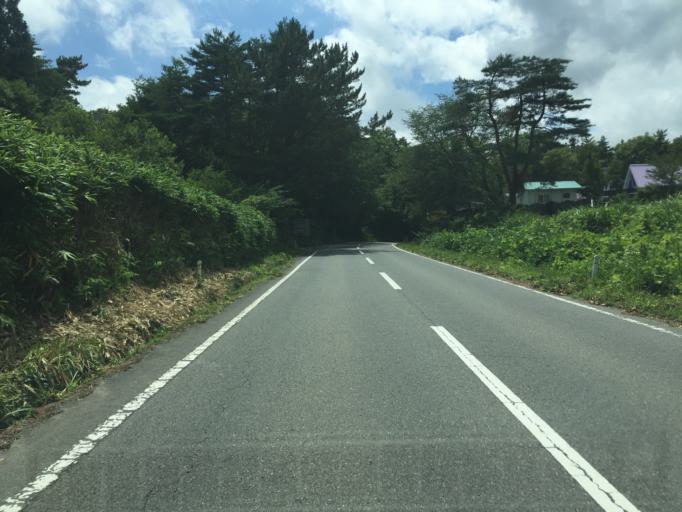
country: JP
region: Fukushima
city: Namie
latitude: 37.6637
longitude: 140.9890
